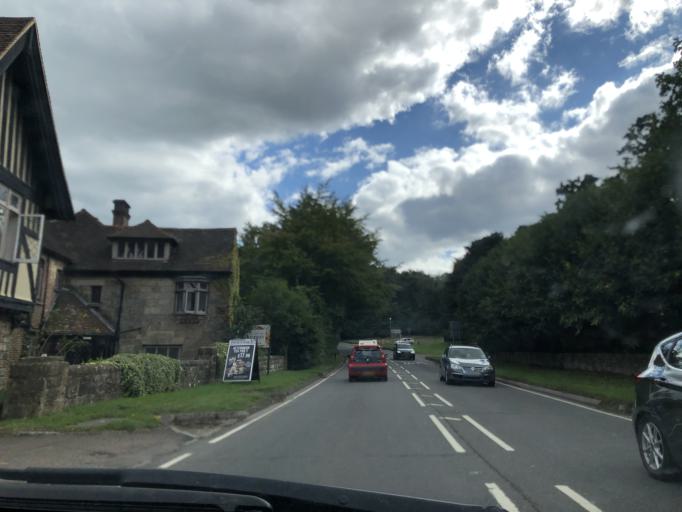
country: GB
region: England
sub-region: East Sussex
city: Forest Row
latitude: 51.0691
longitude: 0.0248
